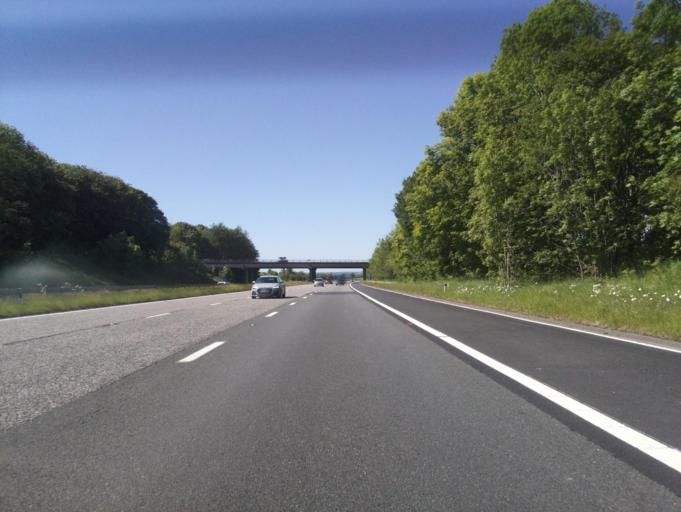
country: GB
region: England
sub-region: Cumbria
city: Penrith
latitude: 54.6120
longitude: -2.7148
